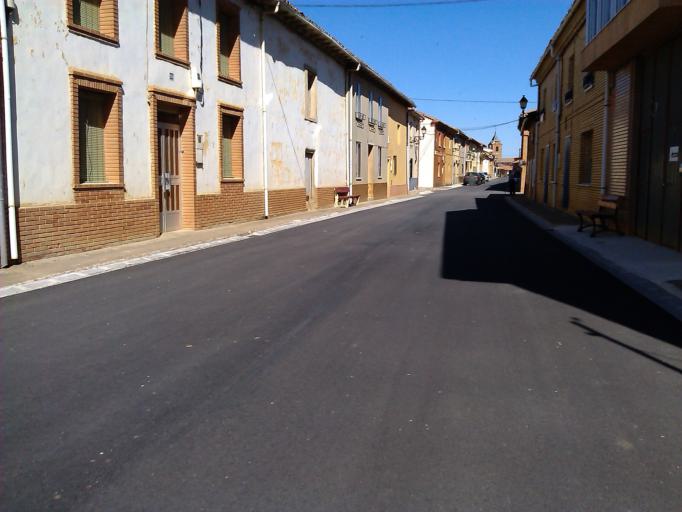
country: ES
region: Castille and Leon
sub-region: Provincia de Leon
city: Vallecillo
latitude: 42.4210
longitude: -5.2172
